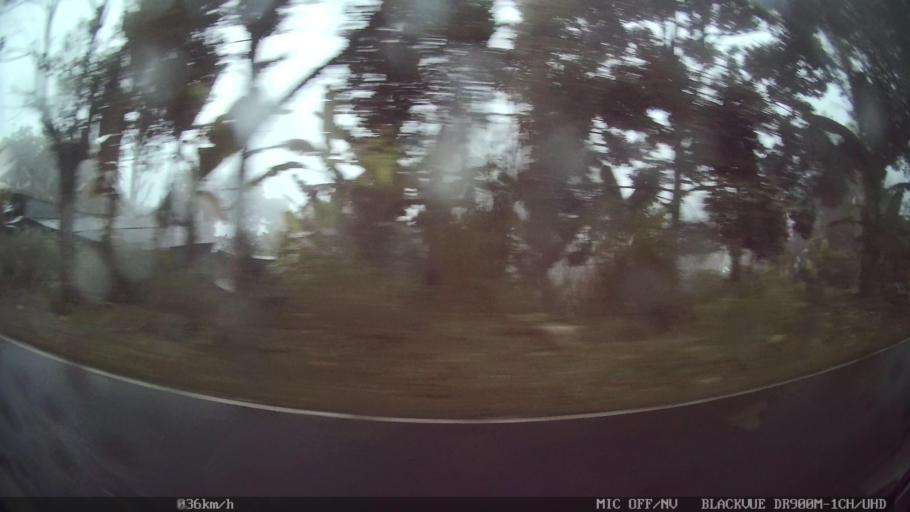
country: ID
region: Bali
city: Banjar Taro Kelod
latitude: -8.3332
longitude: 115.2865
